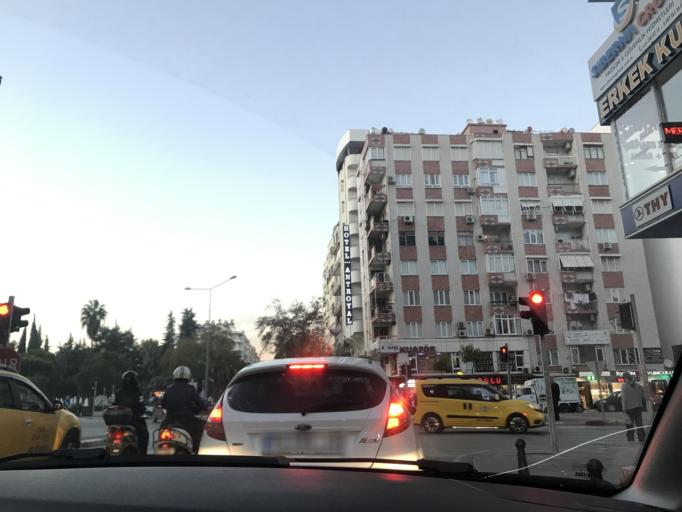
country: TR
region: Antalya
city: Antalya
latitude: 36.8908
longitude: 30.6949
